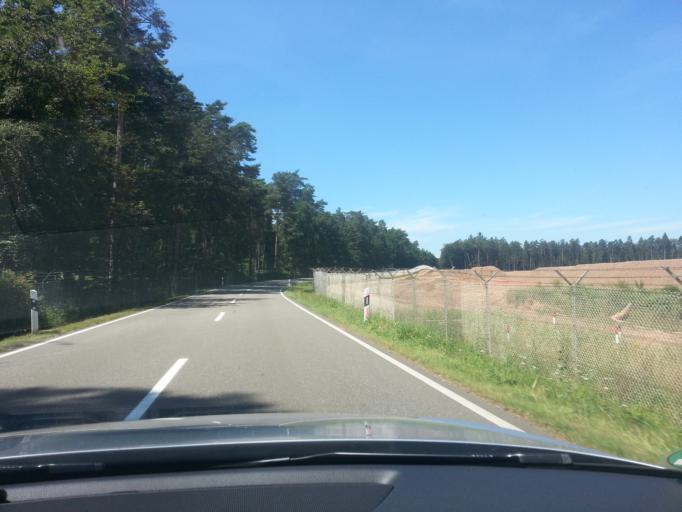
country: DE
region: Rheinland-Pfalz
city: Mackenbach
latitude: 49.4538
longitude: 7.6077
